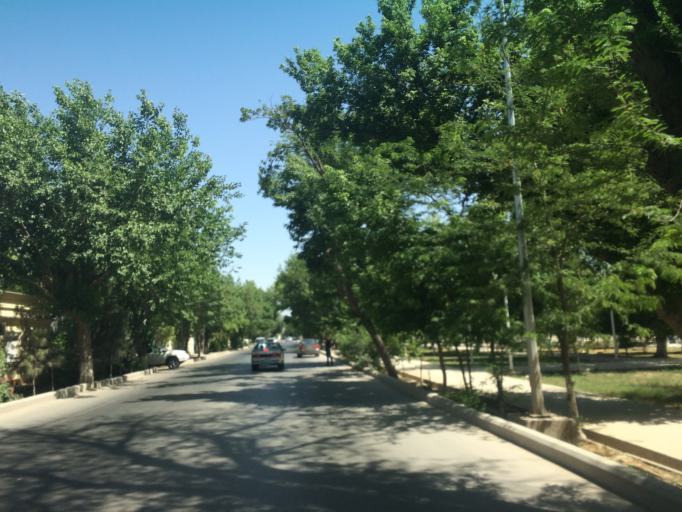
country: TM
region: Ahal
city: Ashgabat
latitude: 37.9475
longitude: 58.3612
